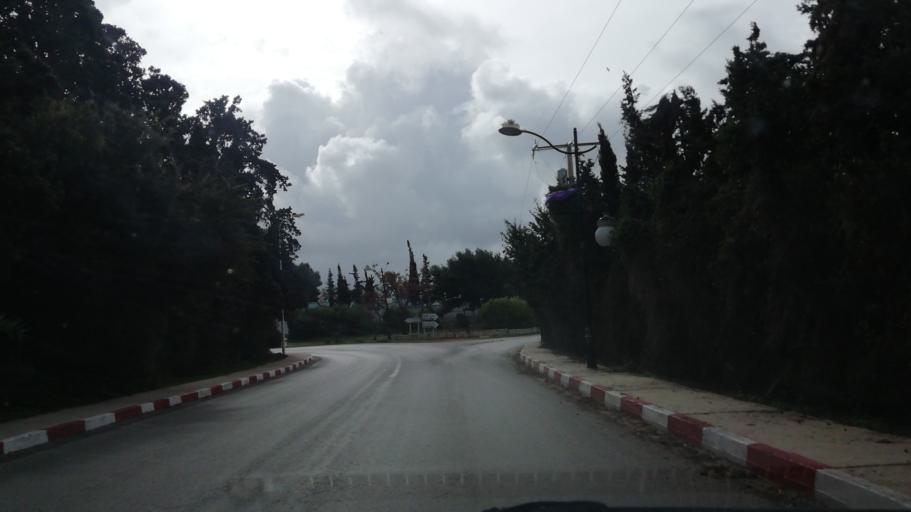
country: DZ
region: Oran
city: Bou Tlelis
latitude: 35.7018
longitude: -0.8925
